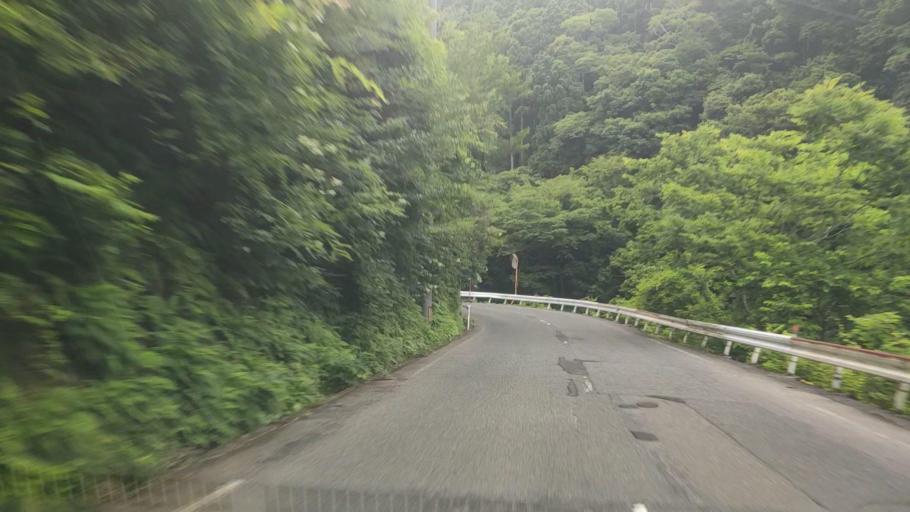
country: JP
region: Tottori
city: Tottori
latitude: 35.3334
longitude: 134.0666
